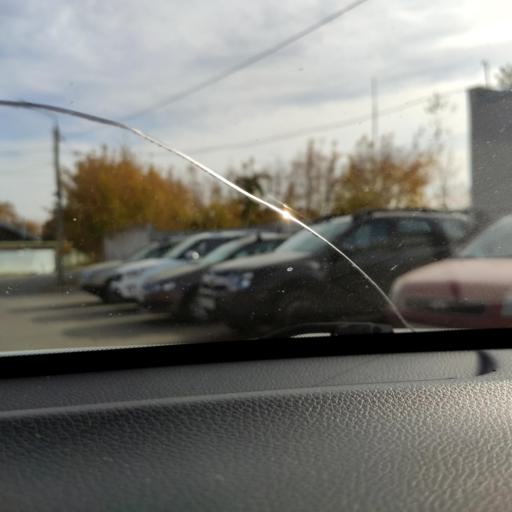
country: RU
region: Tatarstan
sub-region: Gorod Kazan'
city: Kazan
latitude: 55.8071
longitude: 49.0609
